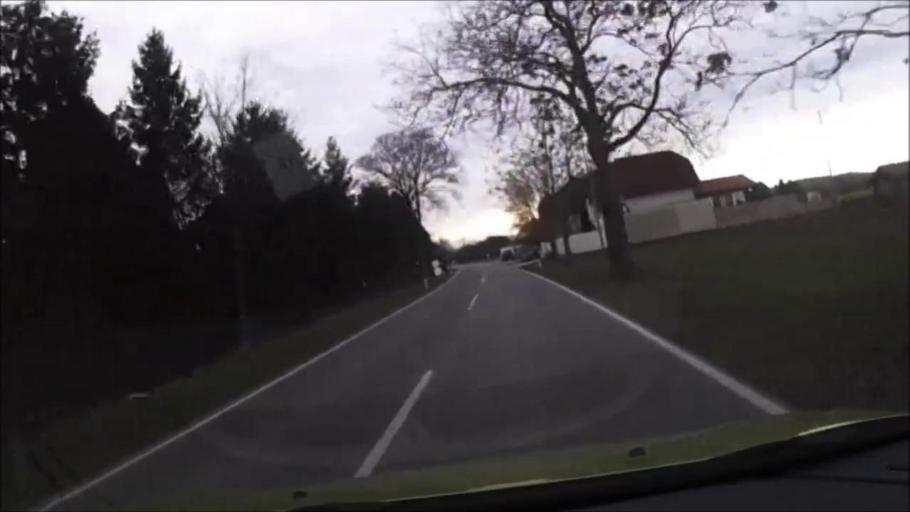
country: AT
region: Burgenland
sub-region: Eisenstadt-Umgebung
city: Wimpassing an der Leitha
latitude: 47.9540
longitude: 16.4388
